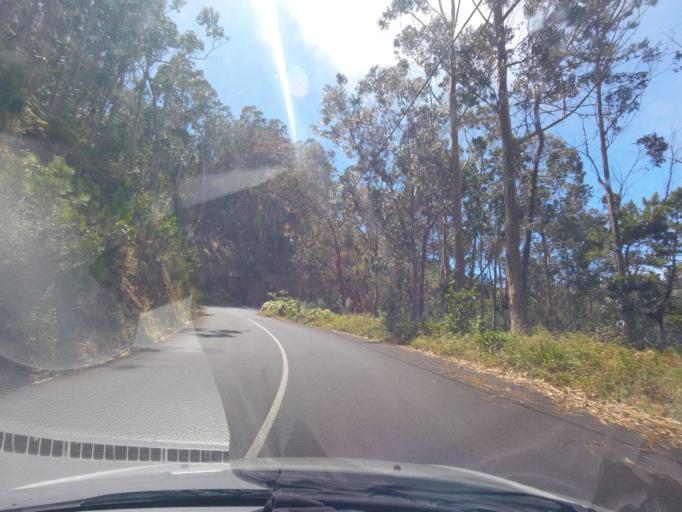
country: PT
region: Madeira
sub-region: Santa Cruz
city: Camacha
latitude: 32.6892
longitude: -16.8310
